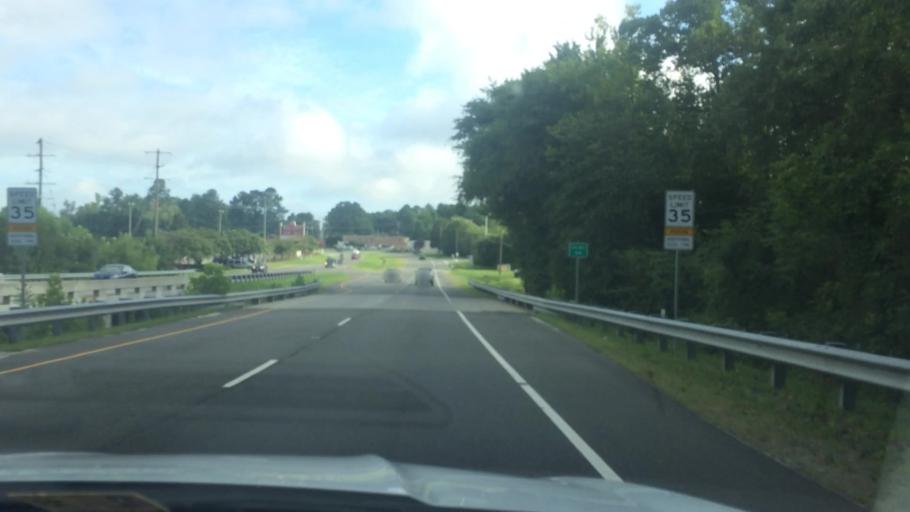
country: US
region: Virginia
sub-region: Gloucester County
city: Gloucester Courthouse
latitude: 37.4078
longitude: -76.5186
